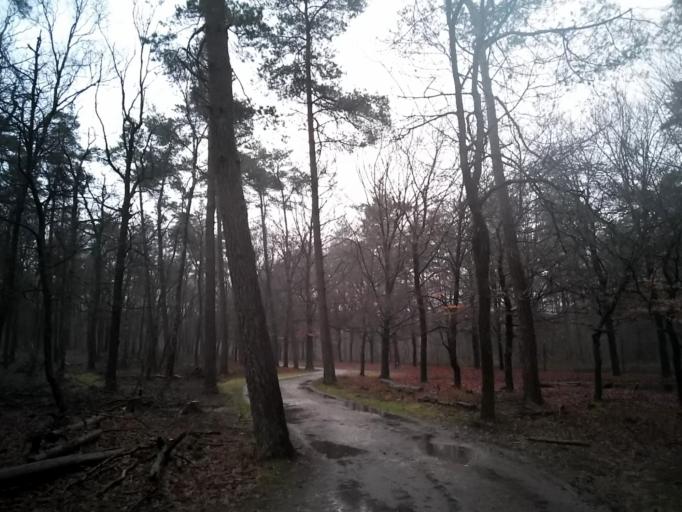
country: NL
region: Gelderland
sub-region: Gemeente Apeldoorn
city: Uddel
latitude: 52.2337
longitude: 5.8356
